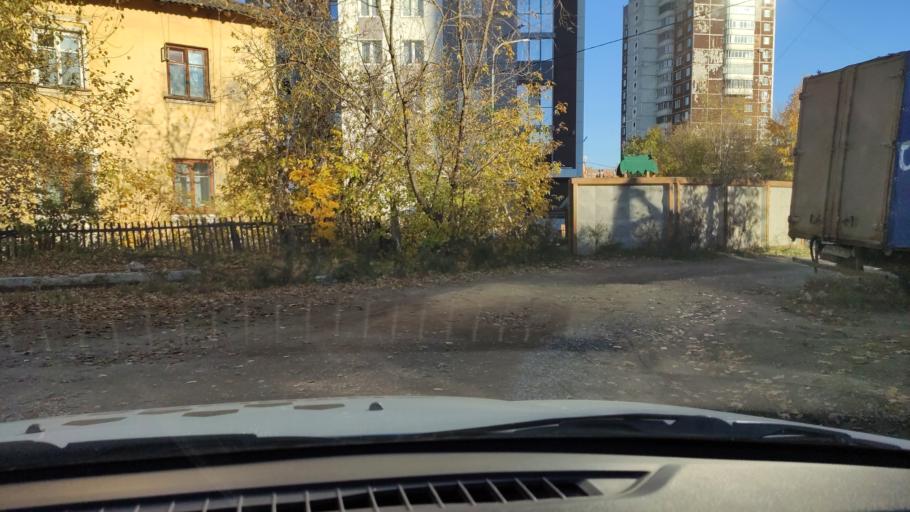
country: RU
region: Perm
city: Kondratovo
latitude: 58.0003
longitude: 56.1552
